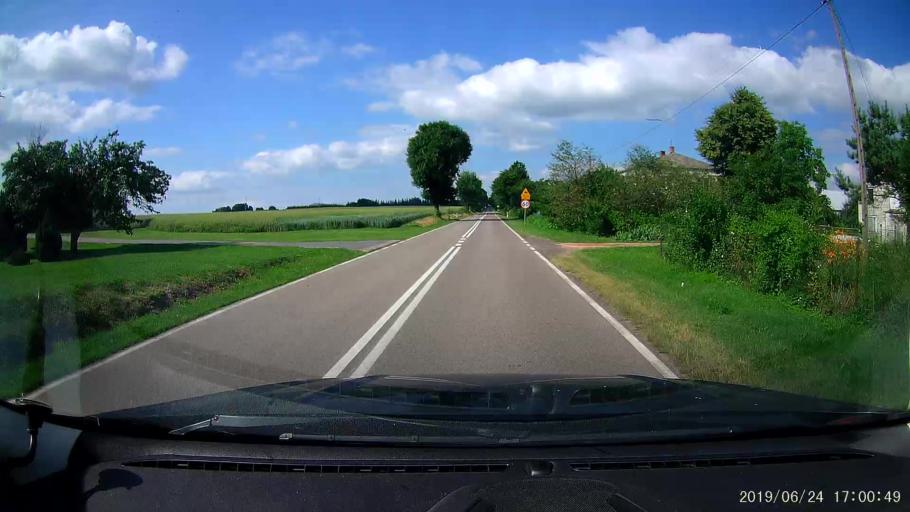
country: PL
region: Lublin Voivodeship
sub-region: Powiat tomaszowski
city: Telatyn
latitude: 50.5321
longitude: 23.9185
